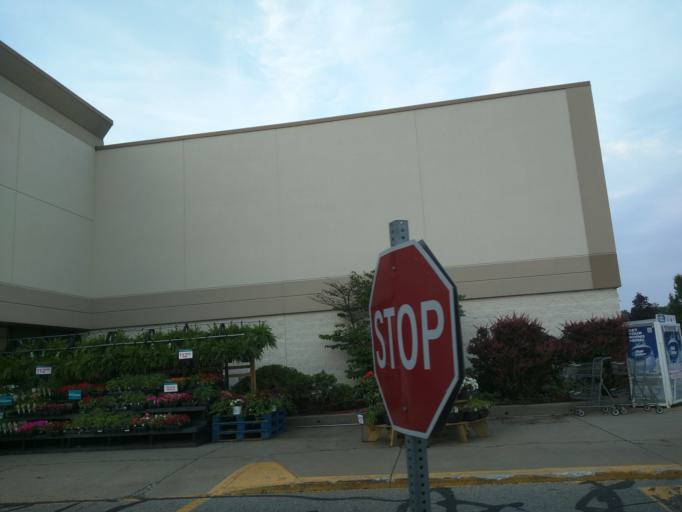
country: US
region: Michigan
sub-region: Ingham County
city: Okemos
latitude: 42.7233
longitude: -84.4133
